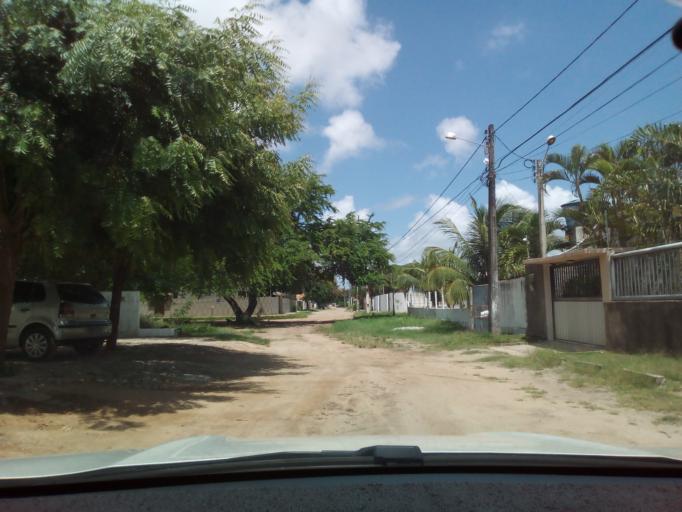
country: BR
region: Paraiba
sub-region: Cabedelo
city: Cabedelo
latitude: -7.0103
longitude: -34.8308
